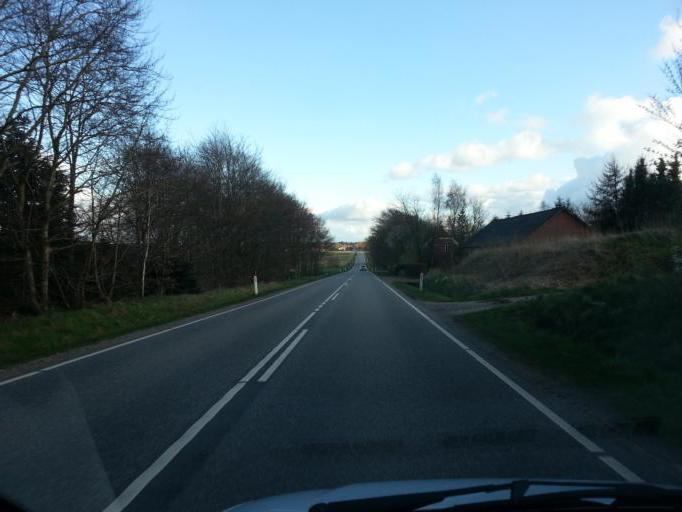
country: DK
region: Central Jutland
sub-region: Ringkobing-Skjern Kommune
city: Tarm
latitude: 55.8631
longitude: 8.5366
